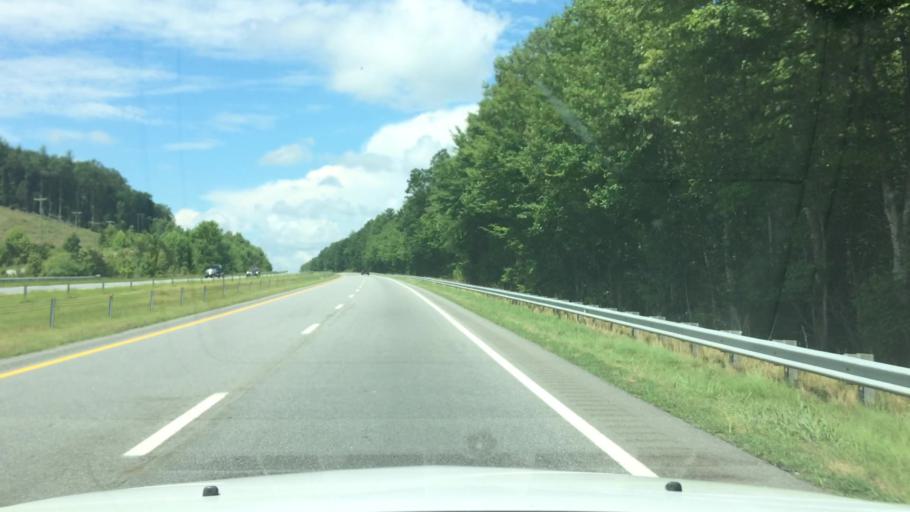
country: US
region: North Carolina
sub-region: Wilkes County
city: North Wilkesboro
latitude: 36.1451
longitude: -81.0562
